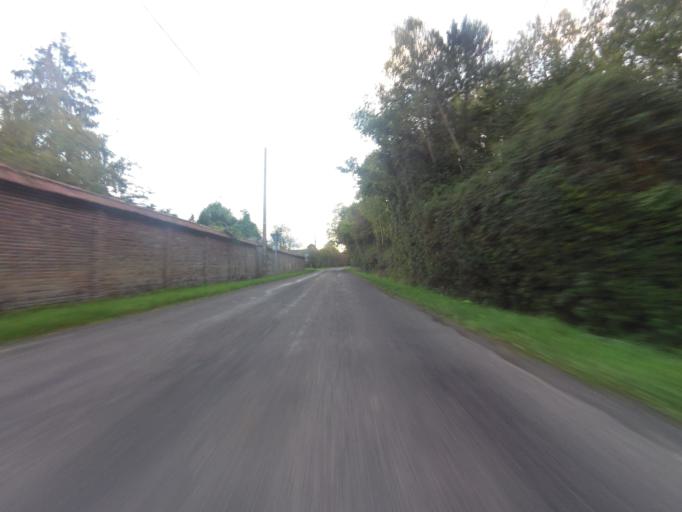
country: FR
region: Lower Normandy
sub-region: Departement de l'Orne
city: Vimoutiers
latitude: 48.9276
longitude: 0.2661
